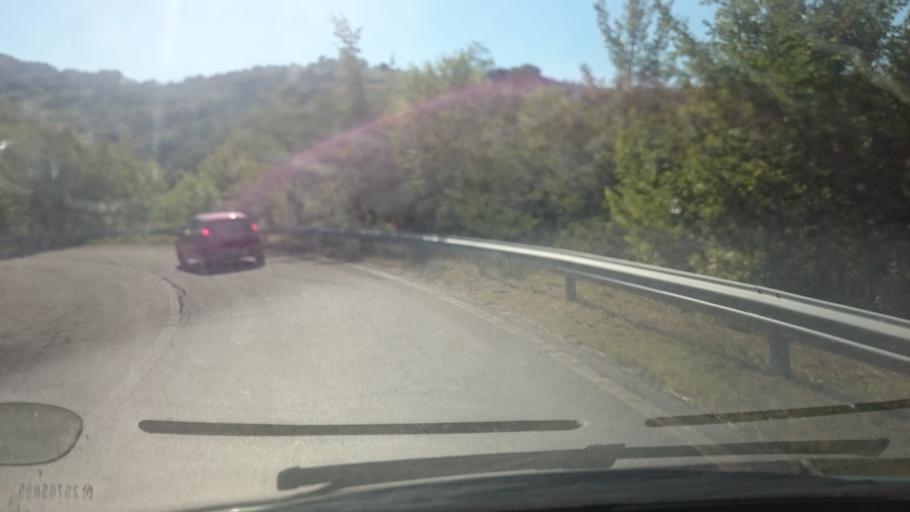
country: IT
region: Emilia-Romagna
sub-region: Provincia di Reggio Emilia
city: Villa Minozzo
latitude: 44.3715
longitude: 10.4596
